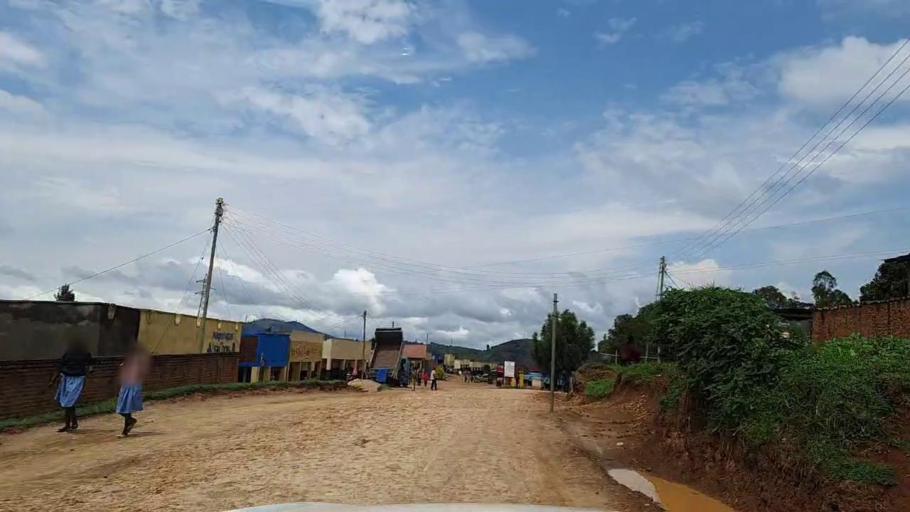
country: RW
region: Southern Province
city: Gikongoro
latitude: -2.3294
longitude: 29.5305
